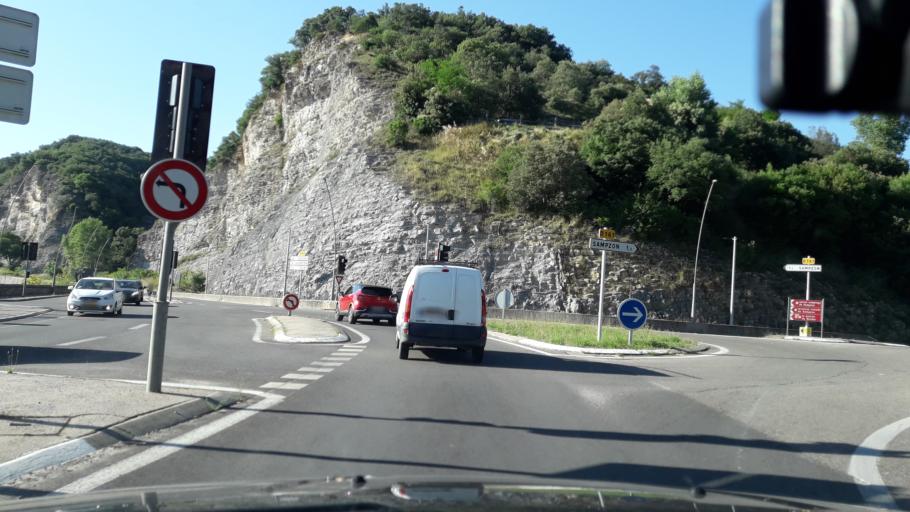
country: FR
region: Rhone-Alpes
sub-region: Departement de l'Ardeche
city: Ruoms
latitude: 44.4294
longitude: 4.3580
